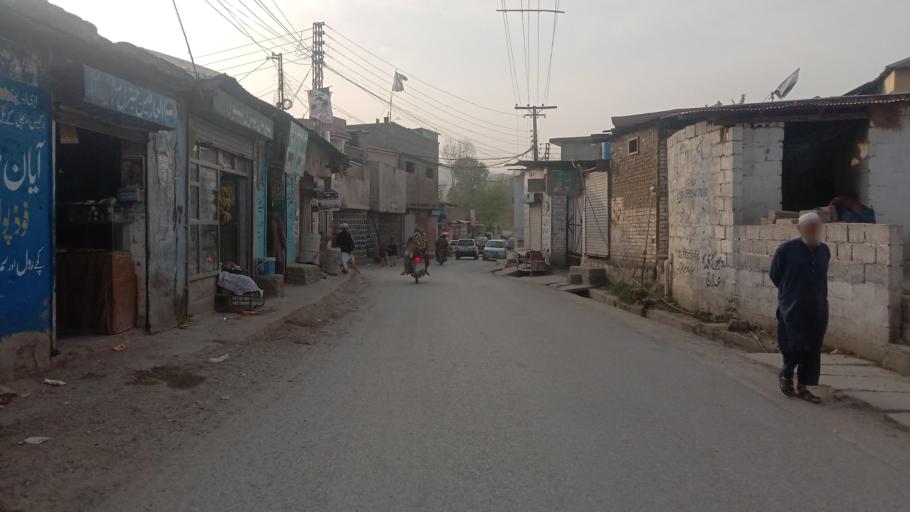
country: PK
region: Khyber Pakhtunkhwa
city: Abbottabad
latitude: 34.1740
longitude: 73.2443
